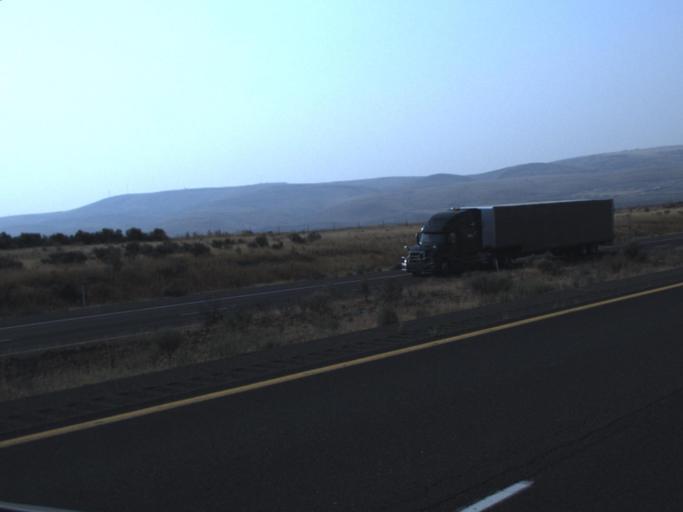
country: US
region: Washington
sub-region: Yakima County
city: Terrace Heights
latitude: 46.6980
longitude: -120.4419
